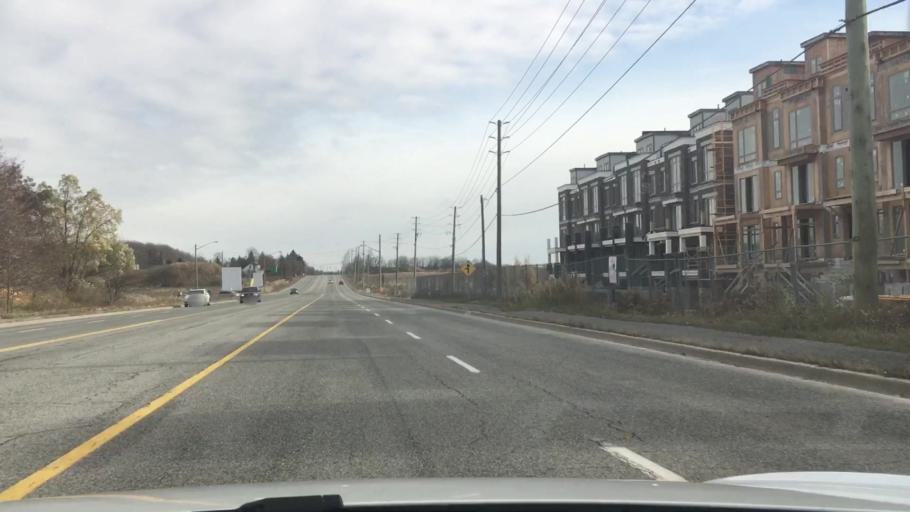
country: CA
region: Ontario
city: Markham
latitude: 43.8793
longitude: -79.2279
